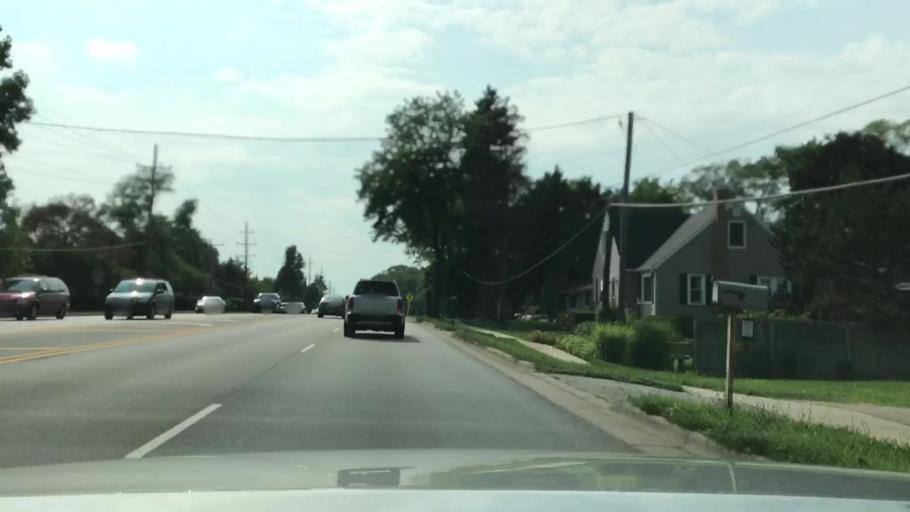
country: US
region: Illinois
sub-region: DuPage County
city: Woodridge
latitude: 41.7727
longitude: -88.0262
